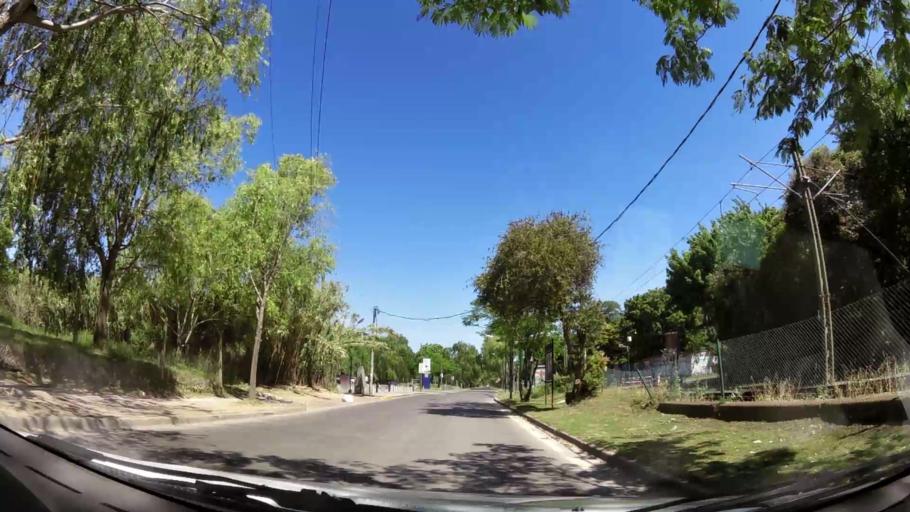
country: AR
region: Buenos Aires
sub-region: Partido de San Isidro
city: San Isidro
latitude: -34.4805
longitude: -58.4830
